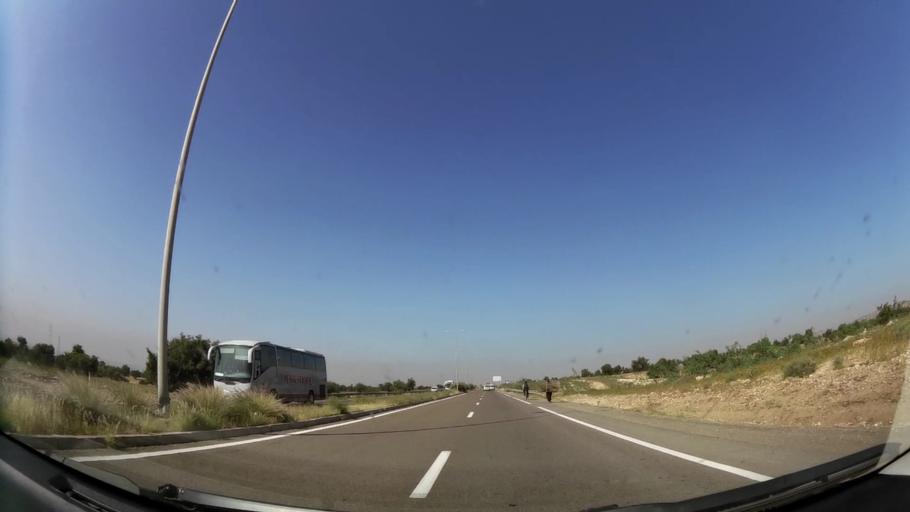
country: MA
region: Souss-Massa-Draa
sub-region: Inezgane-Ait Mellou
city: Inezgane
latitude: 30.4060
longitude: -9.4273
